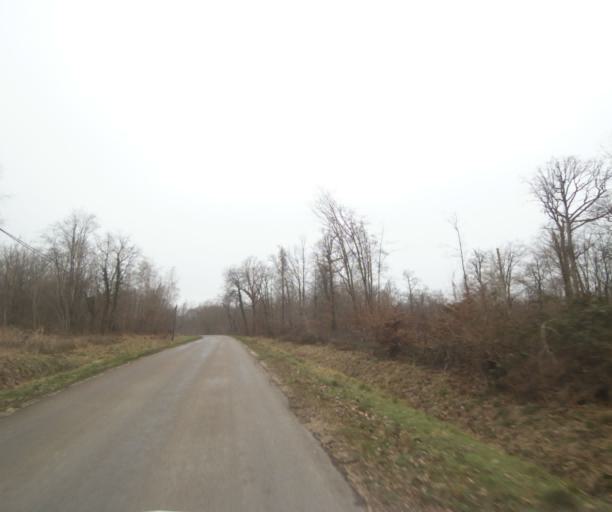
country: FR
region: Champagne-Ardenne
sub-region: Departement de la Haute-Marne
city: Wassy
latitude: 48.5324
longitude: 4.9797
